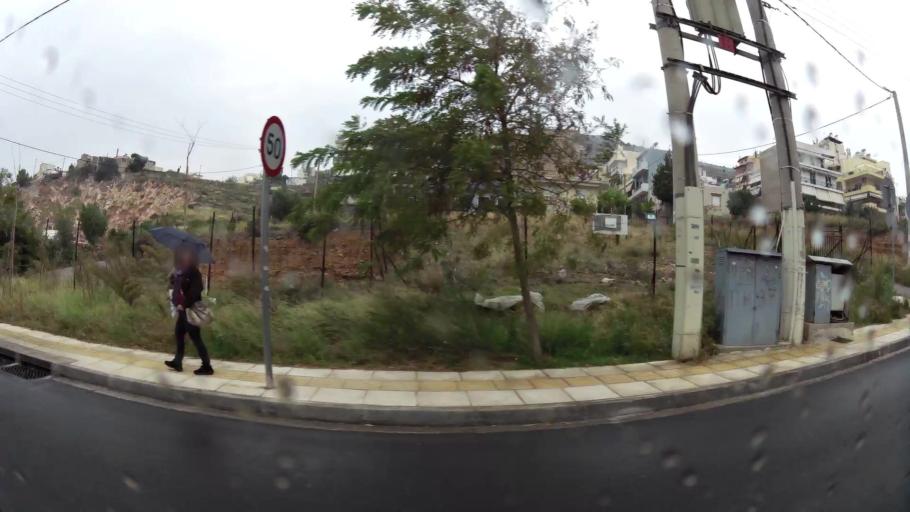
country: GR
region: Attica
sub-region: Nomos Piraios
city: Korydallos
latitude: 37.9906
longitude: 23.6419
